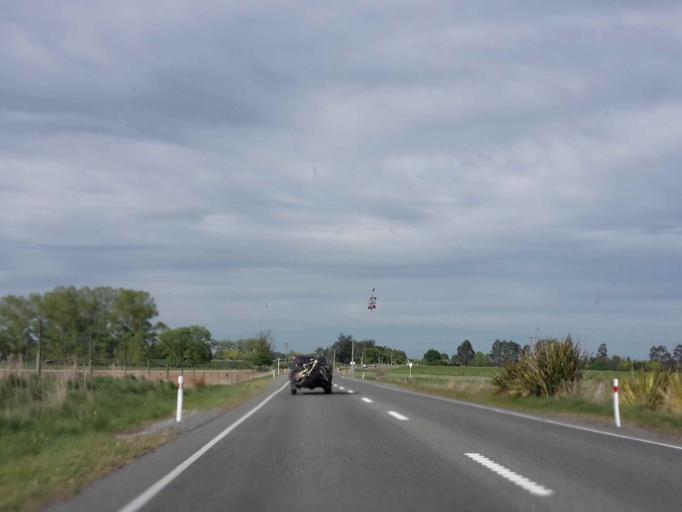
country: NZ
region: Canterbury
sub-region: Timaru District
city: Pleasant Point
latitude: -44.1201
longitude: 171.1967
